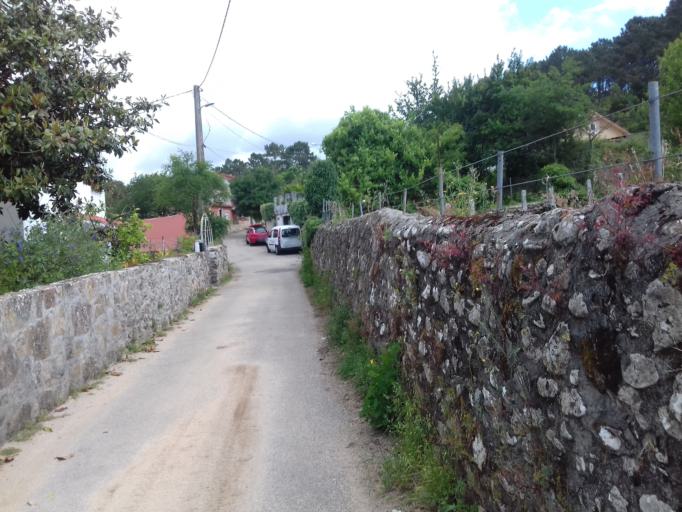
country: ES
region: Galicia
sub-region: Provincia de Pontevedra
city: O Rosal
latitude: 41.9383
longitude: -8.8284
